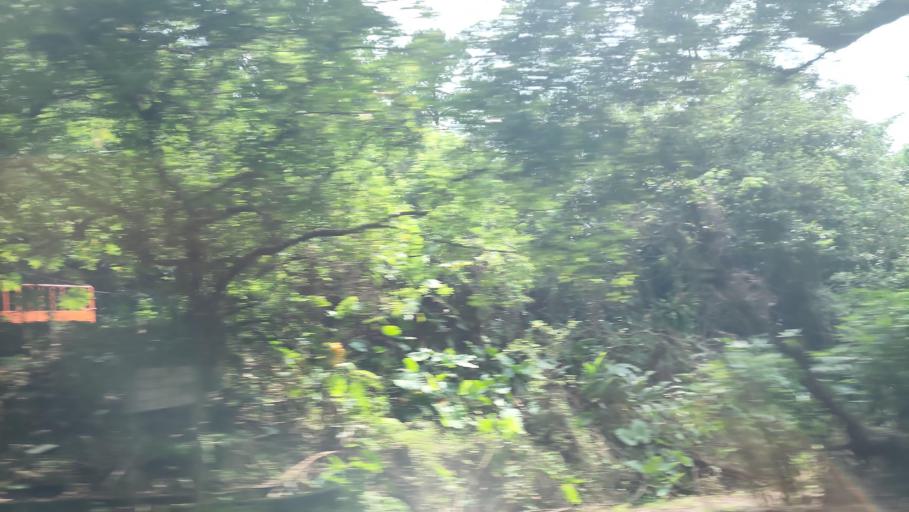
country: TW
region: Taiwan
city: Daxi
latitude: 24.9059
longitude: 121.3980
